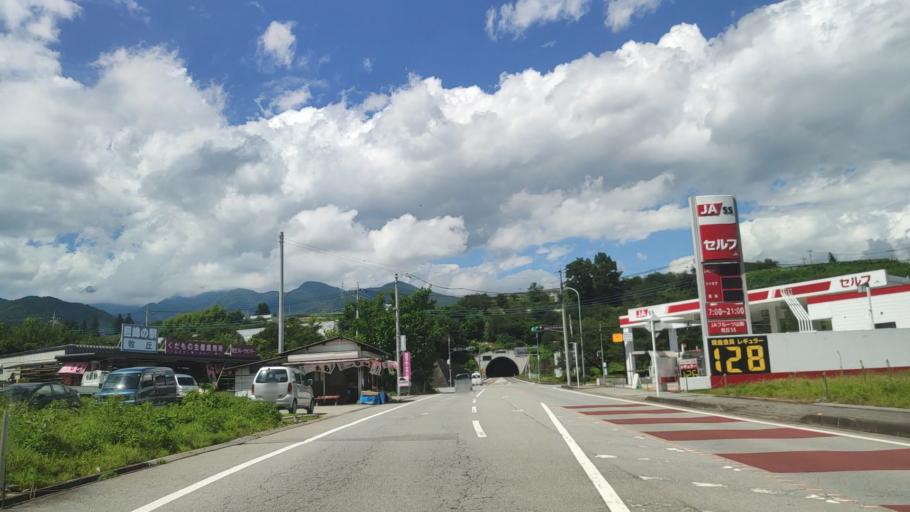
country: JP
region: Yamanashi
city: Enzan
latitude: 35.7415
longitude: 138.7075
